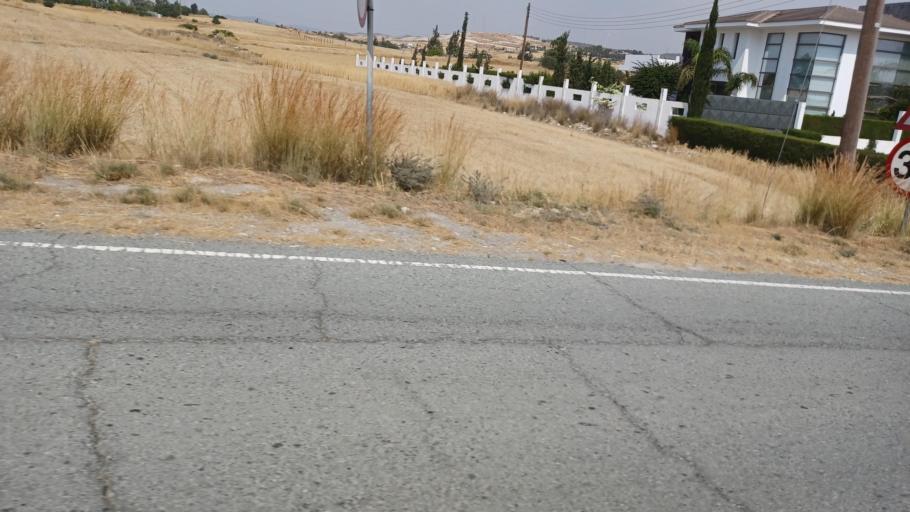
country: CY
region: Larnaka
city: Aradippou
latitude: 34.9446
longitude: 33.5609
